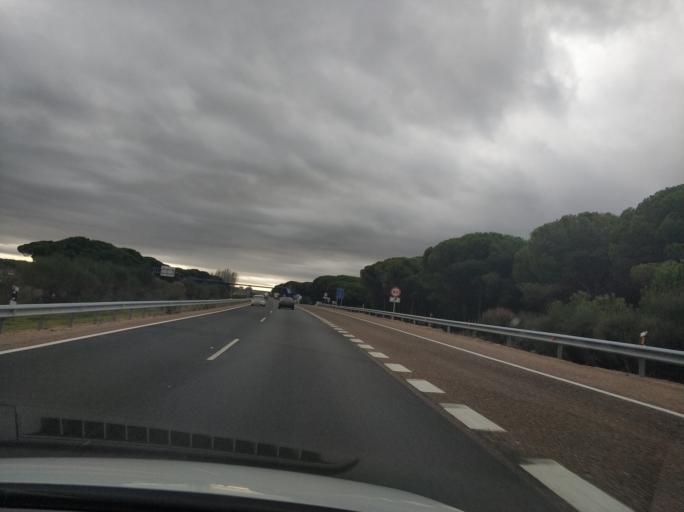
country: ES
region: Castille and Leon
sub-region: Provincia de Valladolid
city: Tordesillas
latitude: 41.4828
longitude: -5.0409
